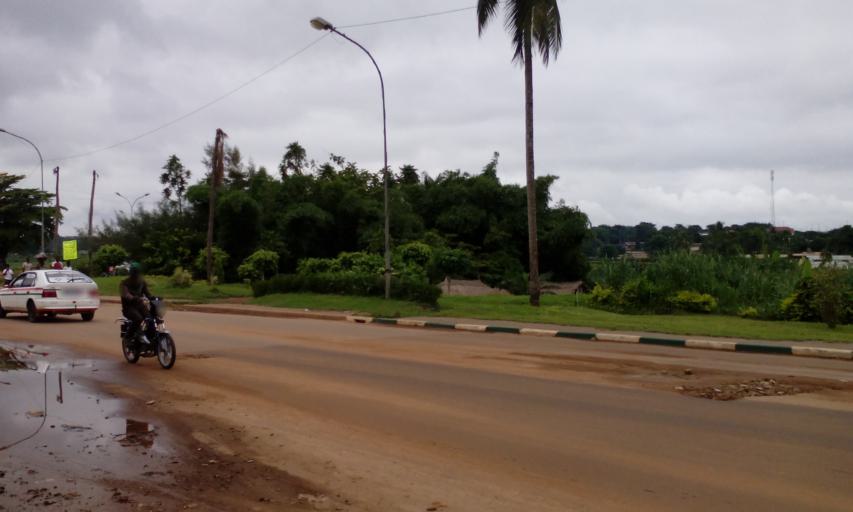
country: CI
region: Lacs
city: Yamoussoukro
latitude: 6.8251
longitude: -5.2672
